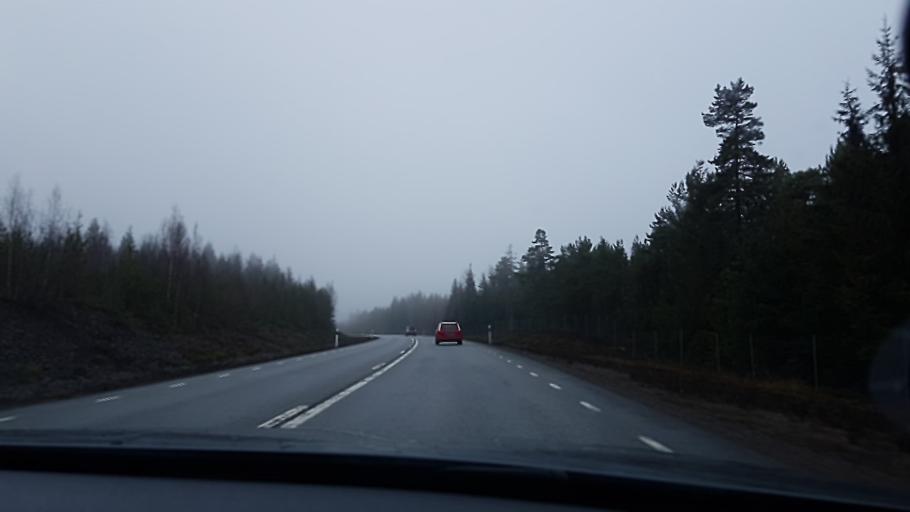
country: SE
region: Vaestra Goetaland
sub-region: Gullspangs Kommun
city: Gullspang
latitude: 58.8747
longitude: 14.0086
